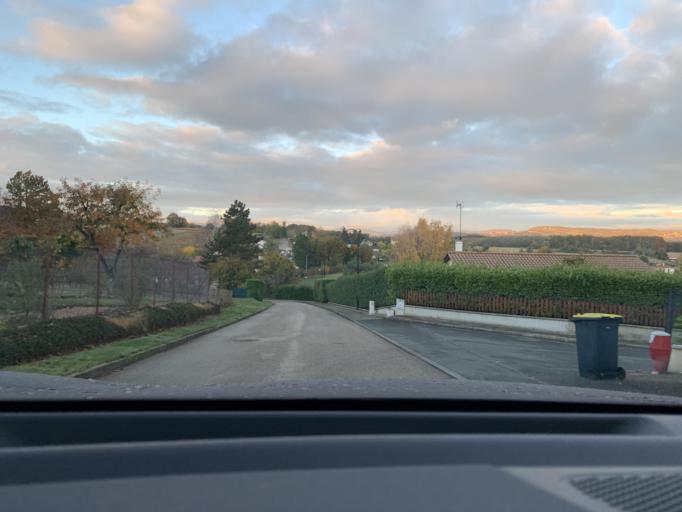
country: FR
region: Rhone-Alpes
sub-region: Departement du Rhone
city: Charnay
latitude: 45.9162
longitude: 4.6761
